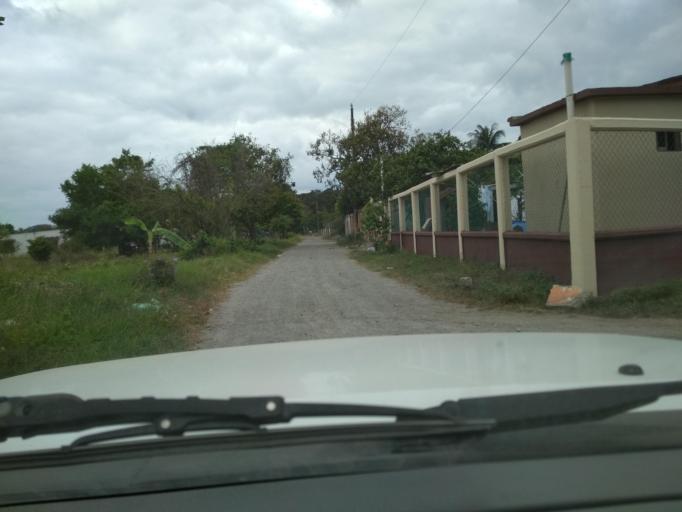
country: MX
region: Veracruz
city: El Tejar
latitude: 19.0735
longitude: -96.1503
